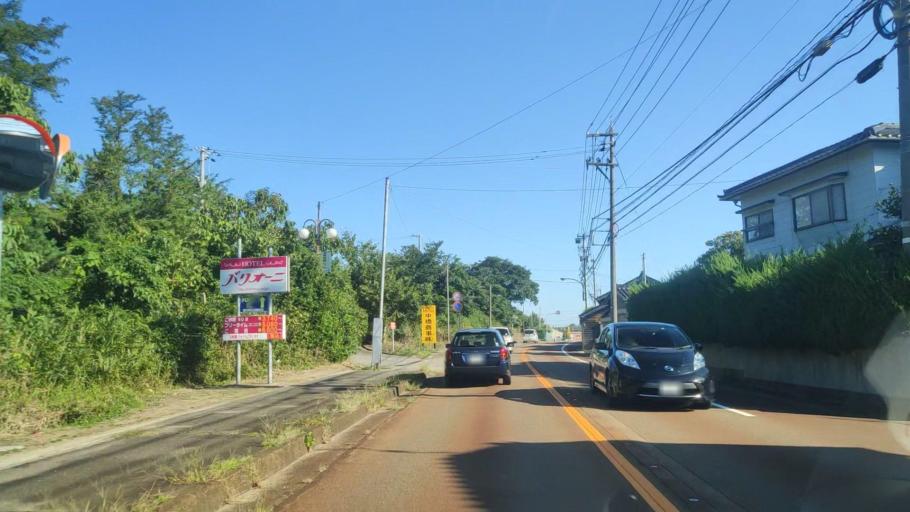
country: JP
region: Ishikawa
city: Hakui
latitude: 36.8580
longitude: 136.7696
